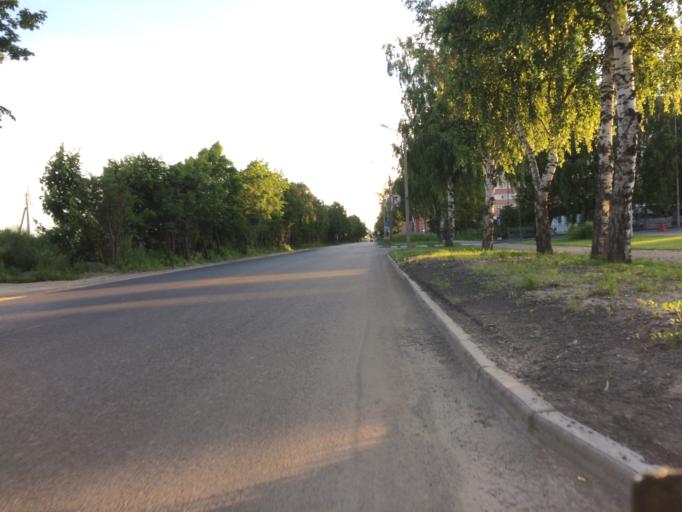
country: RU
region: Mariy-El
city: Medvedevo
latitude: 56.6431
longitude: 47.8315
